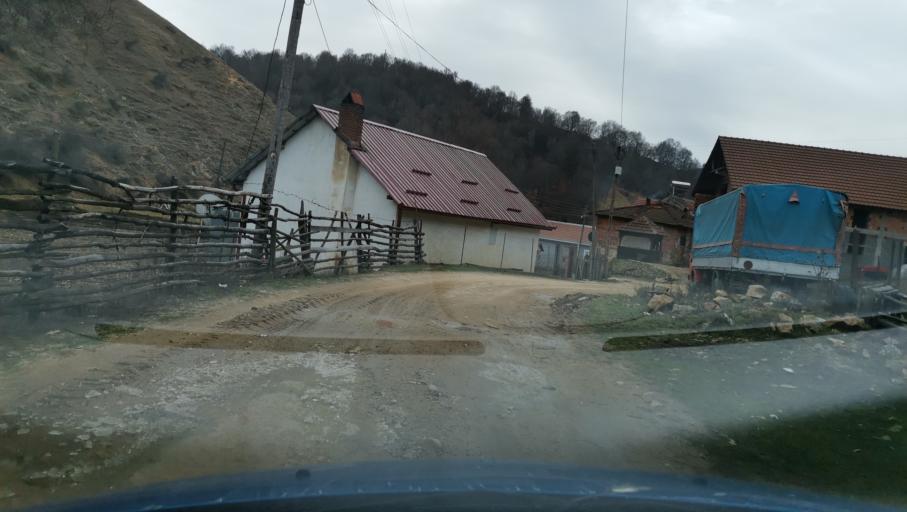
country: MK
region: Berovo
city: Berovo
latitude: 41.5917
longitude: 22.9189
